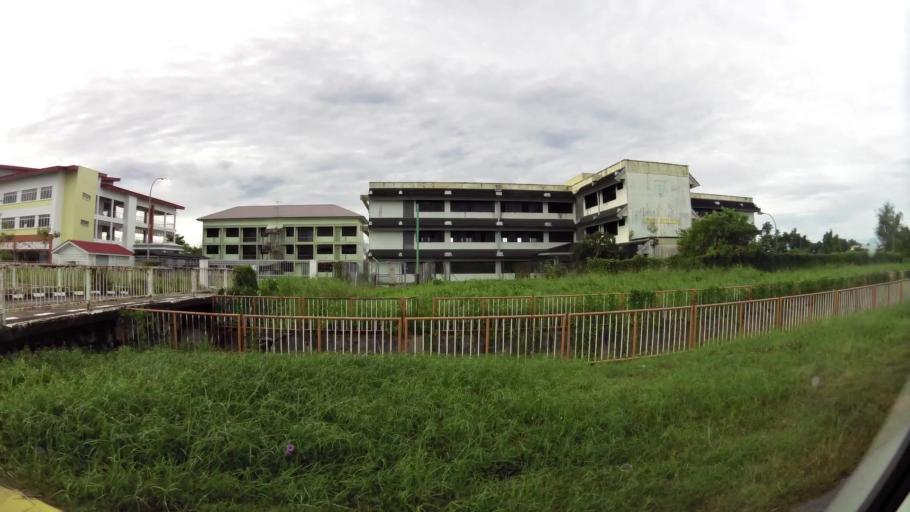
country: BN
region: Belait
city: Seria
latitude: 4.6081
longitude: 114.3310
